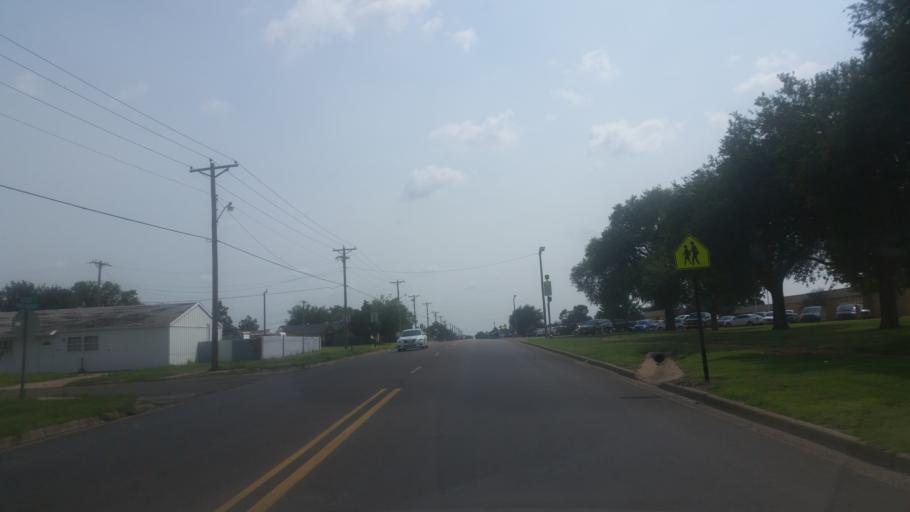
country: US
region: New Mexico
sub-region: Curry County
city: Clovis
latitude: 34.4186
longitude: -103.2142
